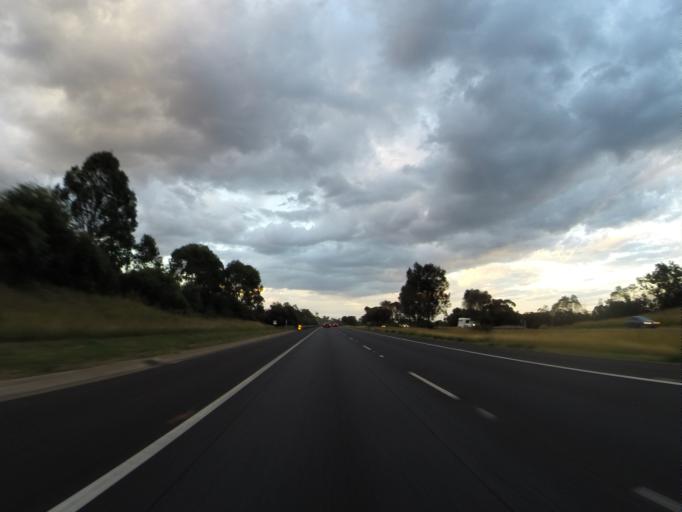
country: AU
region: New South Wales
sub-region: Campbelltown Municipality
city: Glen Alpine
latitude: -34.0746
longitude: 150.7757
